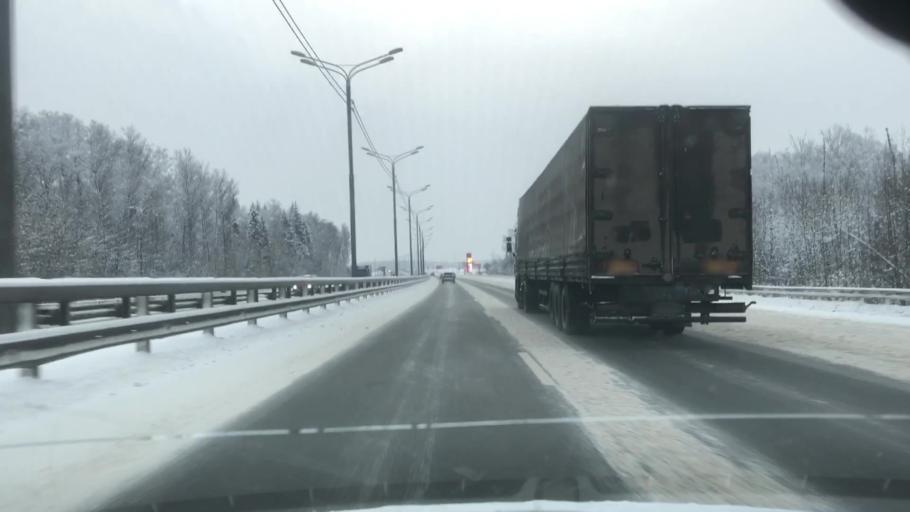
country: RU
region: Moskovskaya
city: Barybino
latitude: 55.2001
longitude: 37.8883
